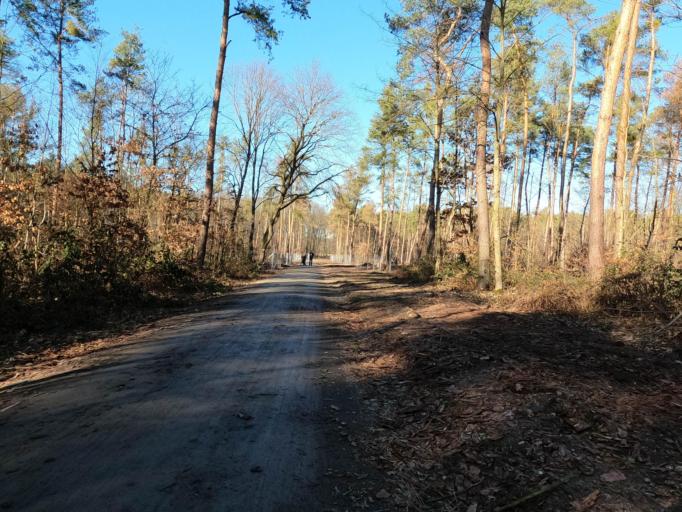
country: DE
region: Hesse
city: Kelsterbach
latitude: 50.0734
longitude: 8.5655
